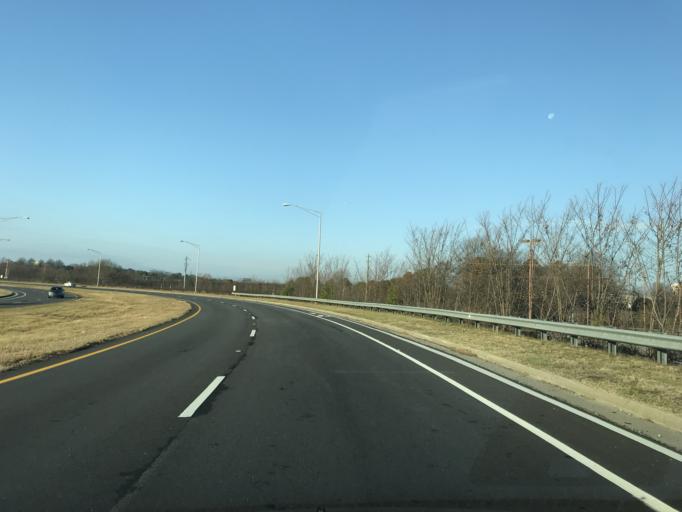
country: US
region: Georgia
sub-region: Fulton County
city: College Park
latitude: 33.6220
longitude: -84.4503
